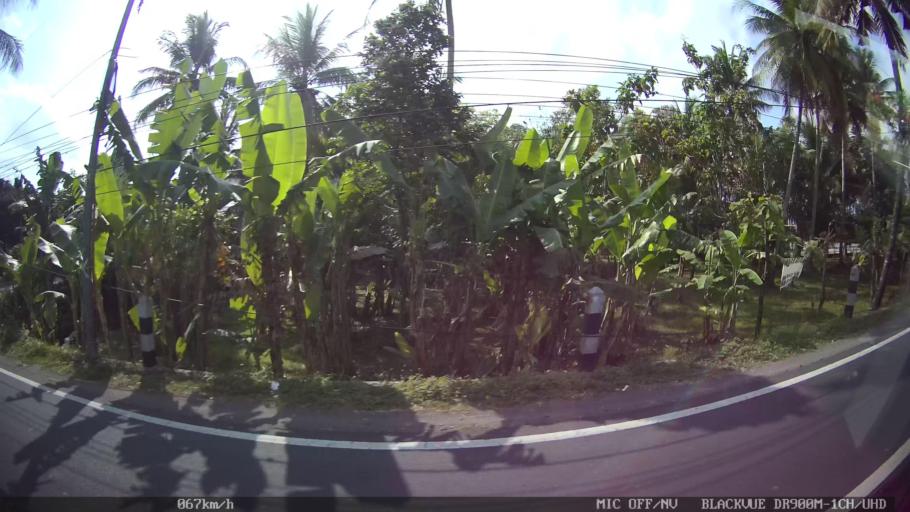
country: ID
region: Daerah Istimewa Yogyakarta
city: Srandakan
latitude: -7.8711
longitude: 110.2088
